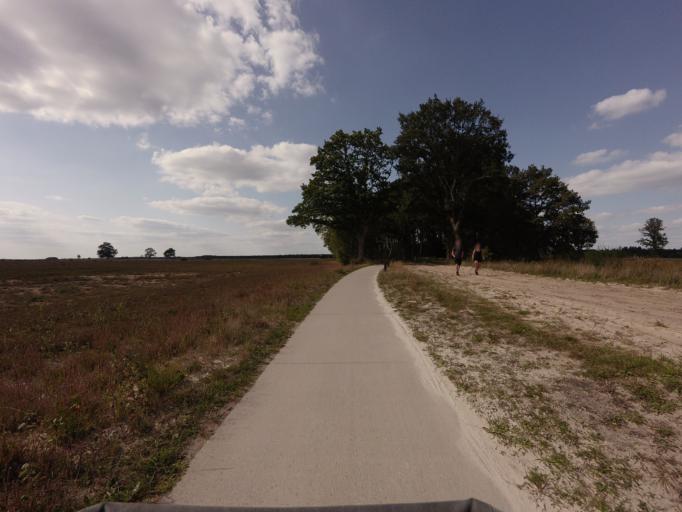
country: NL
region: Drenthe
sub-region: Gemeente Westerveld
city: Dwingeloo
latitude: 52.8048
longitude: 6.4139
